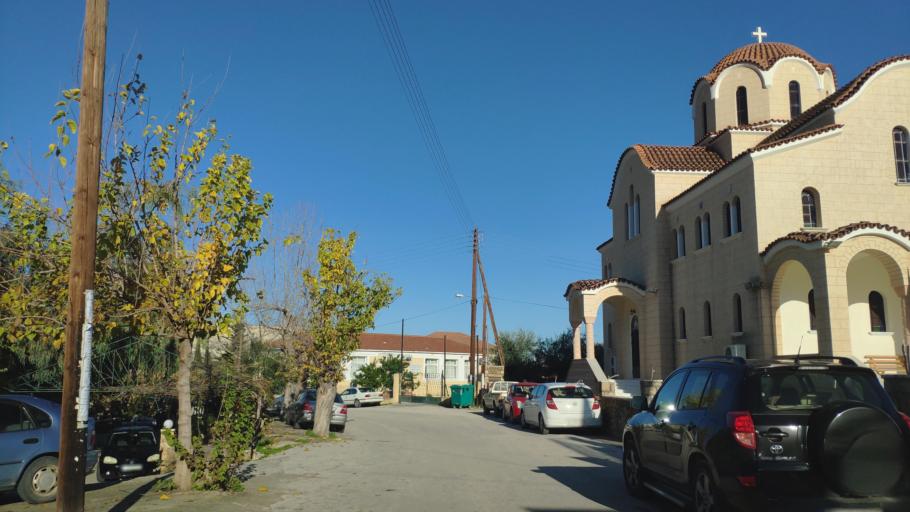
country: GR
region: Peloponnese
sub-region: Nomos Korinthias
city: Xylokastro
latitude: 38.0454
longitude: 22.5860
